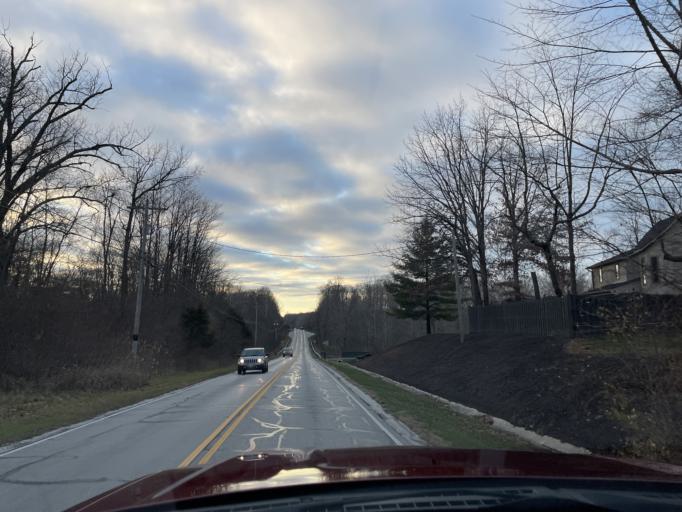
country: US
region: Indiana
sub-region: Hendricks County
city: Avon
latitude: 39.7771
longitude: -86.4116
